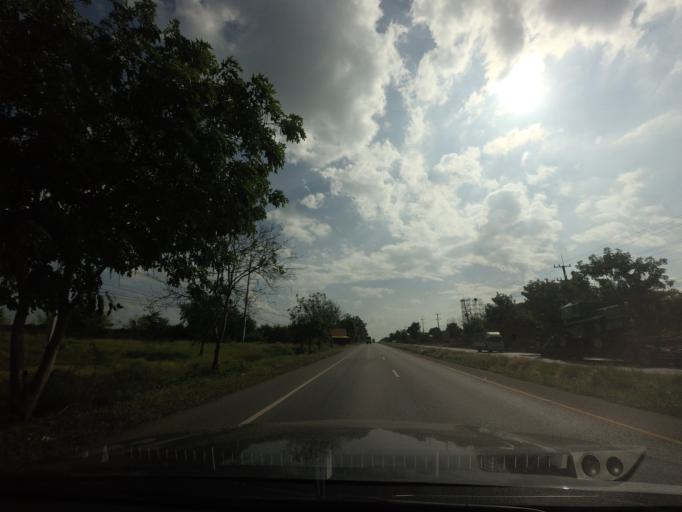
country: TH
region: Lop Buri
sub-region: Amphoe Tha Luang
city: Tha Luang
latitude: 15.1374
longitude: 101.0439
